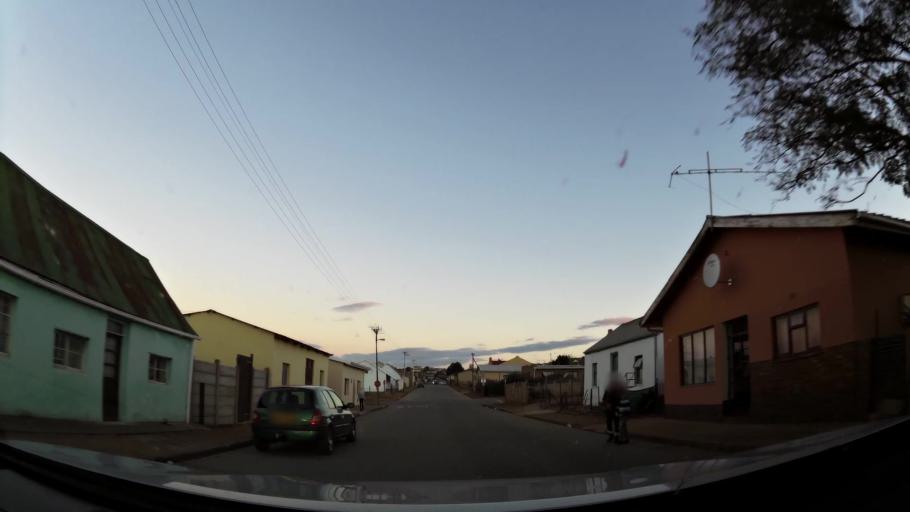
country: ZA
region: Western Cape
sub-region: Eden District Municipality
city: Riversdale
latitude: -34.0961
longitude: 21.2621
